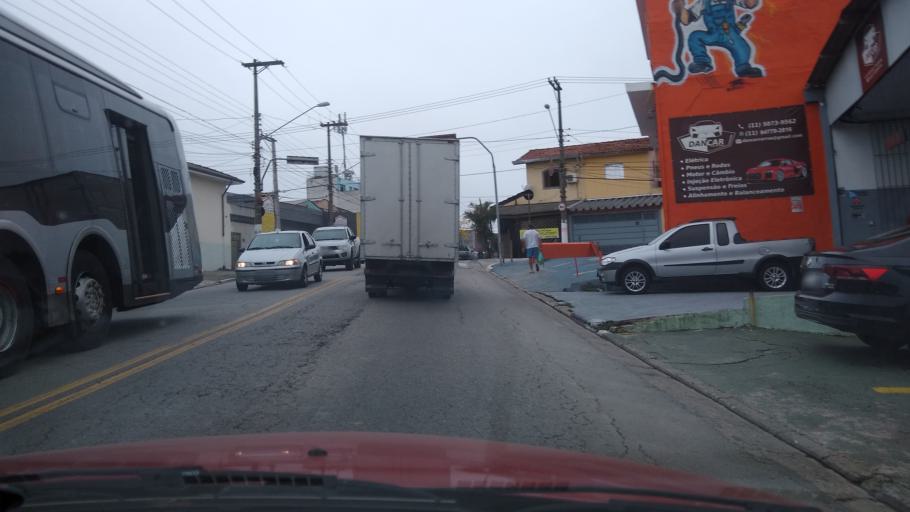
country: BR
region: Sao Paulo
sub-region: Diadema
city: Diadema
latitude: -23.6354
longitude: -46.6152
